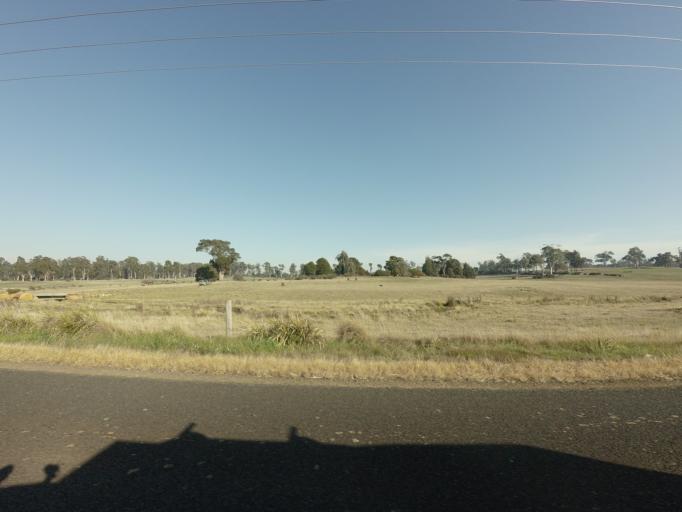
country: AU
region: Tasmania
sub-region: Northern Midlands
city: Longford
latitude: -41.5436
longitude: 146.9918
